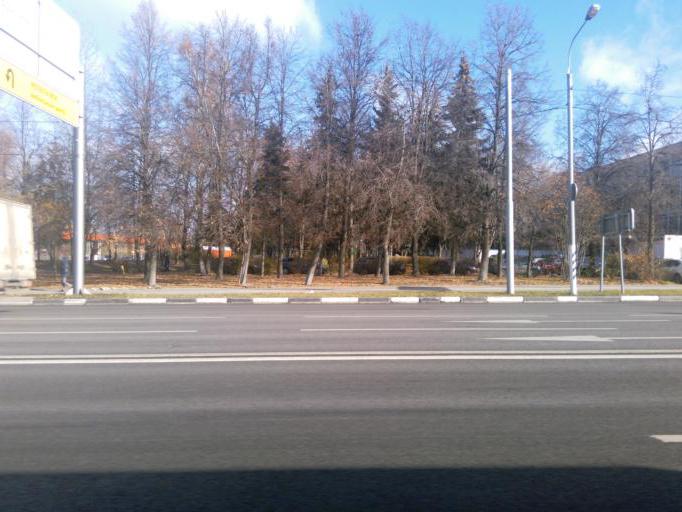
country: RU
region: Moskovskaya
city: Cheremushki
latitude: 55.6539
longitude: 37.5434
